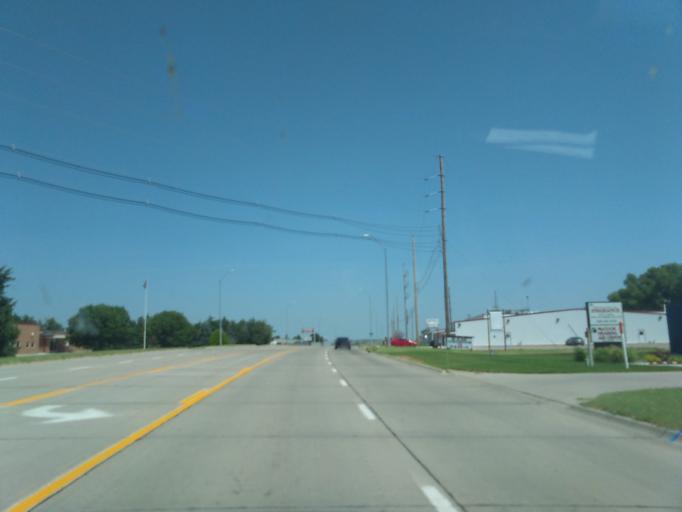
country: US
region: Nebraska
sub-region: Red Willow County
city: McCook
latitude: 40.2125
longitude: -100.6501
